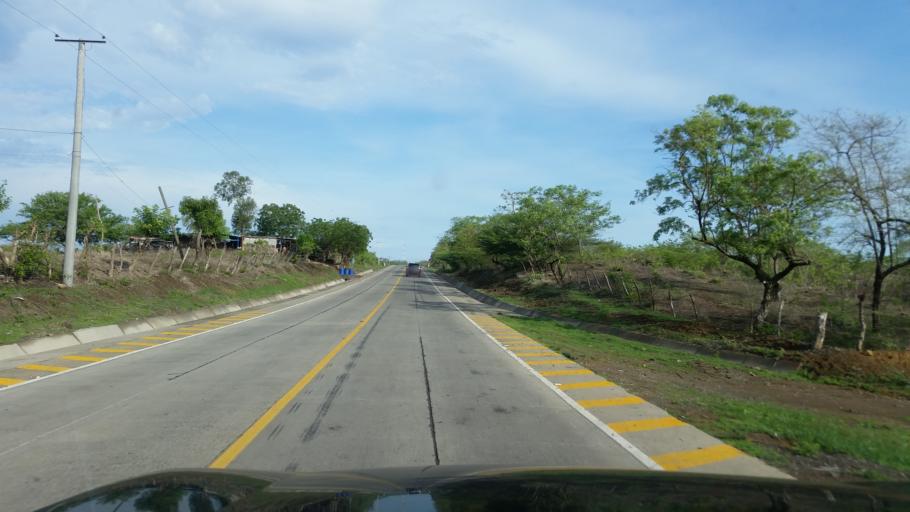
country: NI
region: Leon
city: Nagarote
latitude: 12.1119
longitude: -86.6023
